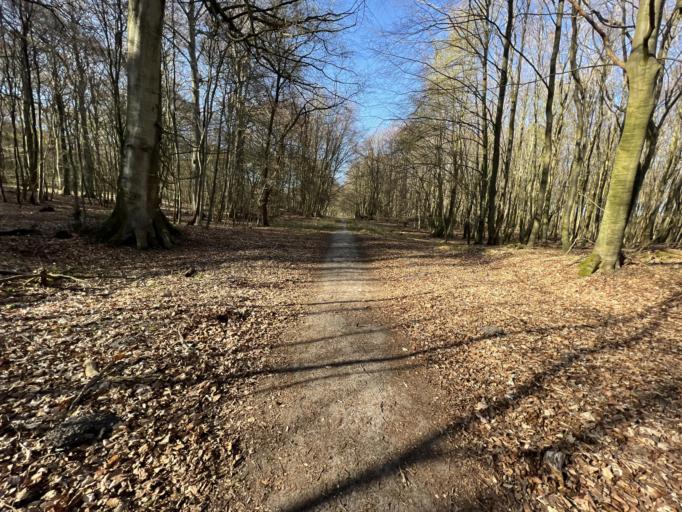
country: DE
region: Mecklenburg-Vorpommern
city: Sassnitz
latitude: 54.5309
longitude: 13.6428
